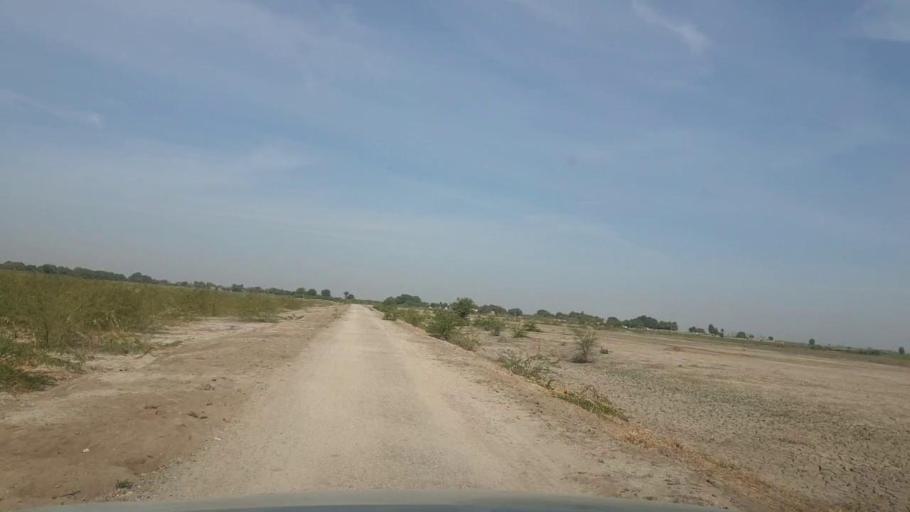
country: PK
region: Sindh
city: Nabisar
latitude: 25.1163
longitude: 69.6071
